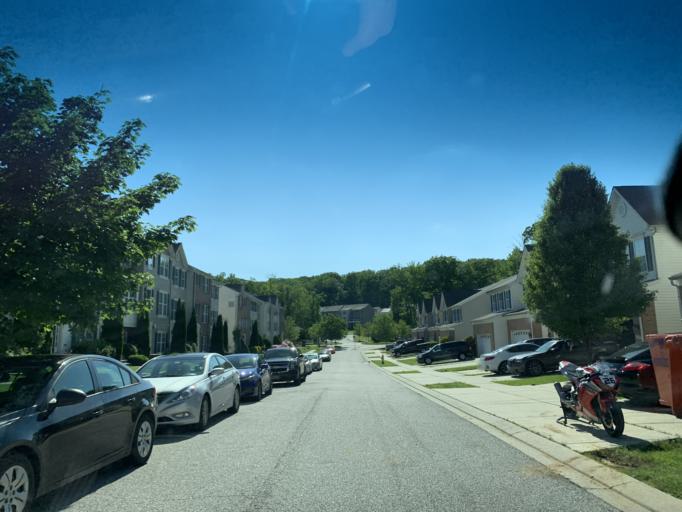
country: US
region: Maryland
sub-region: Harford County
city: Riverside
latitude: 39.4957
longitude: -76.2224
